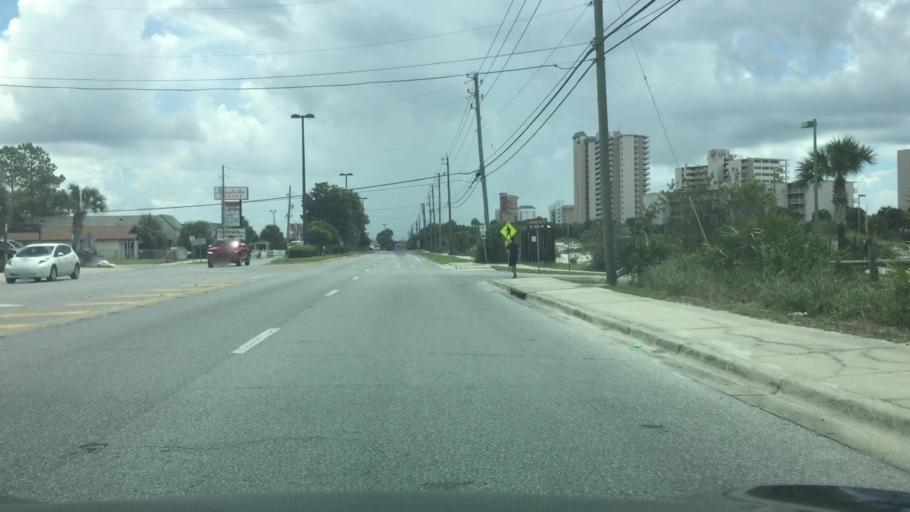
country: US
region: Florida
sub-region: Bay County
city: Lower Grand Lagoon
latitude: 30.1602
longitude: -85.7781
